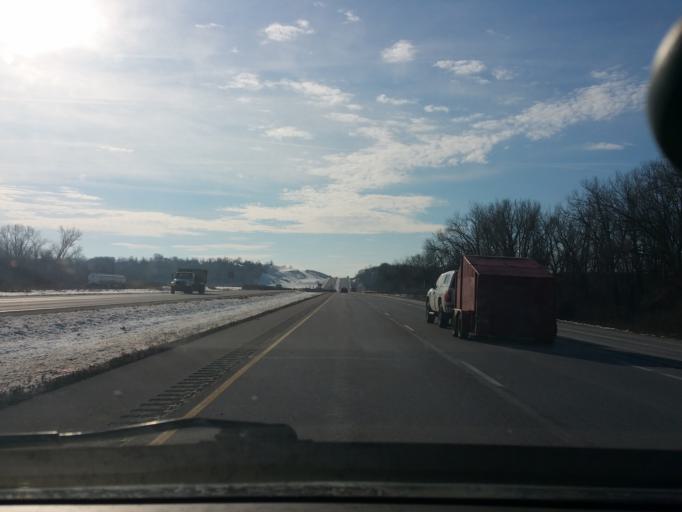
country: US
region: Iowa
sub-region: Warren County
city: Norwalk
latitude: 41.3596
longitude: -93.7801
